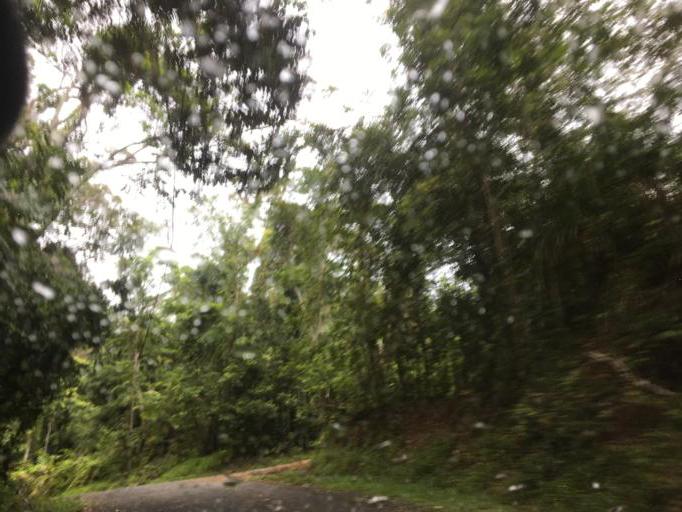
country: AU
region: Queensland
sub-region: Tablelands
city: Kuranda
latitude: -16.8401
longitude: 145.6422
